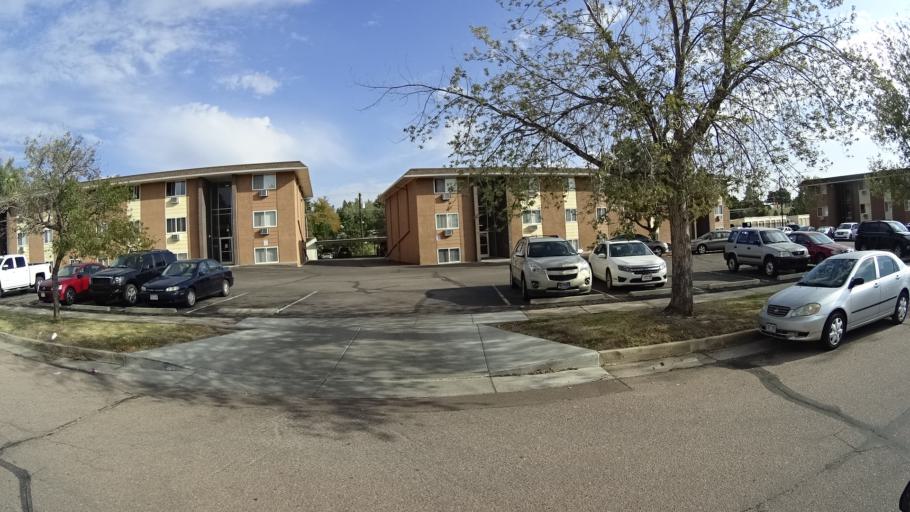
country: US
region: Colorado
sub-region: El Paso County
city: Cimarron Hills
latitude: 38.8584
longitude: -104.7615
